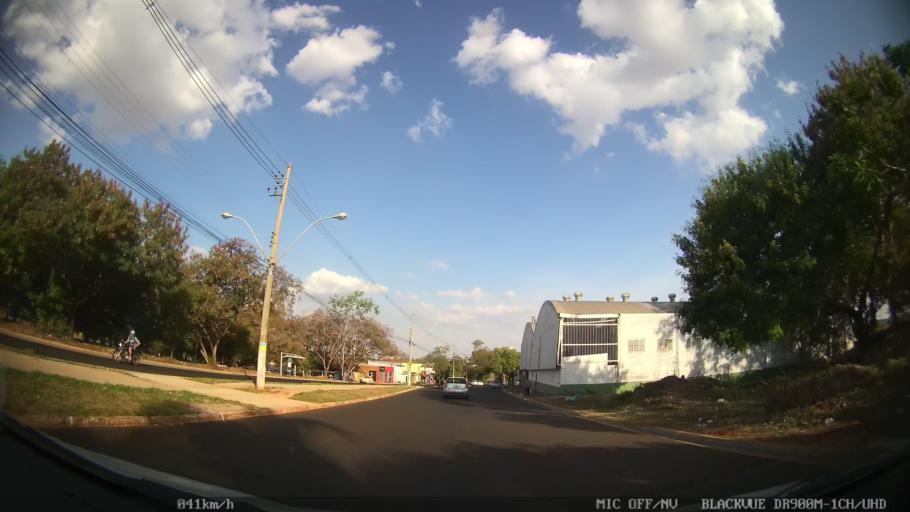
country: BR
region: Sao Paulo
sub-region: Ribeirao Preto
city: Ribeirao Preto
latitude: -21.1408
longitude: -47.8336
